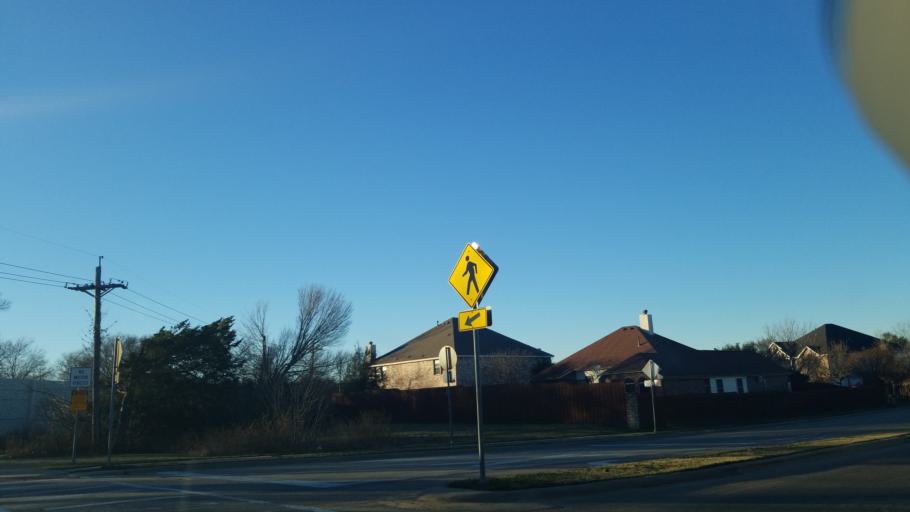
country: US
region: Texas
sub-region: Denton County
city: Hickory Creek
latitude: 33.1446
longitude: -97.0425
